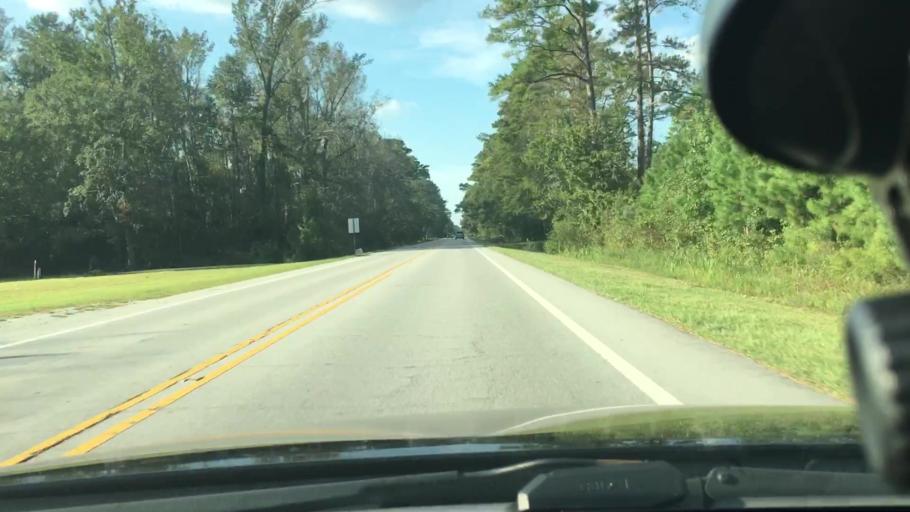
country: US
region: North Carolina
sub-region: Craven County
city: New Bern
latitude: 35.1601
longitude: -77.0382
